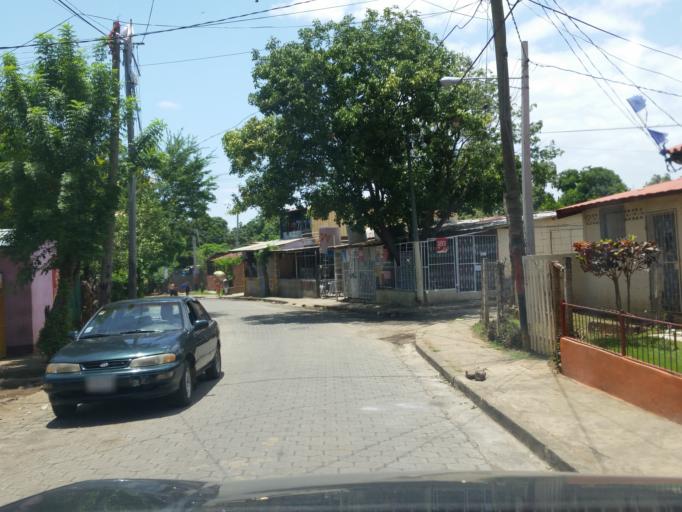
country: NI
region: Managua
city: Managua
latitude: 12.1182
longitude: -86.2461
